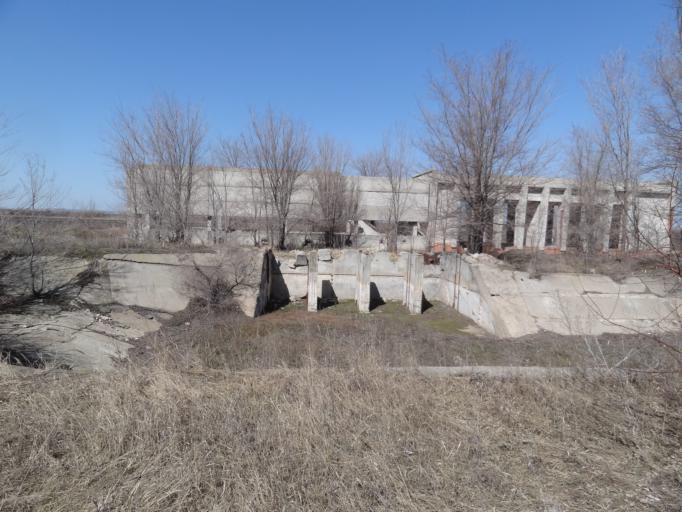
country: RU
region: Saratov
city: Shumeyka
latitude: 51.4096
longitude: 46.2445
